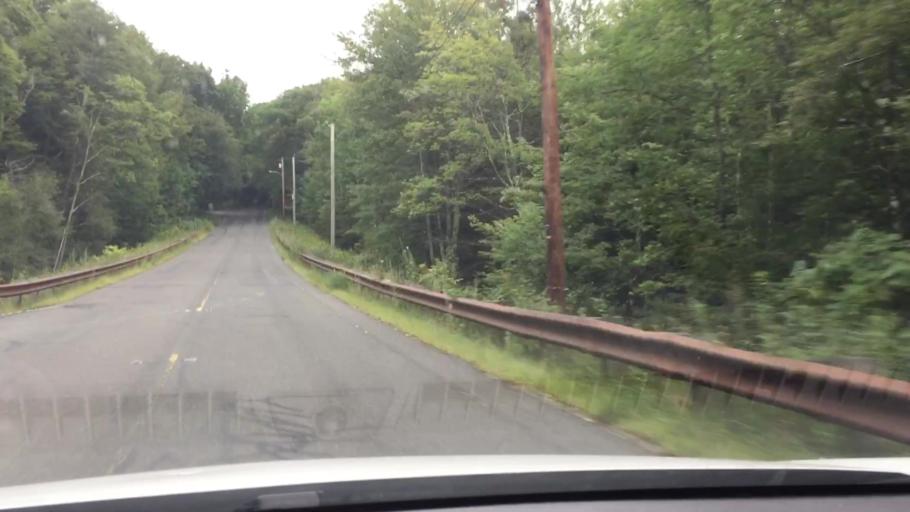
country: US
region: Massachusetts
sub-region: Berkshire County
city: Otis
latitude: 42.2502
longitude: -72.9918
